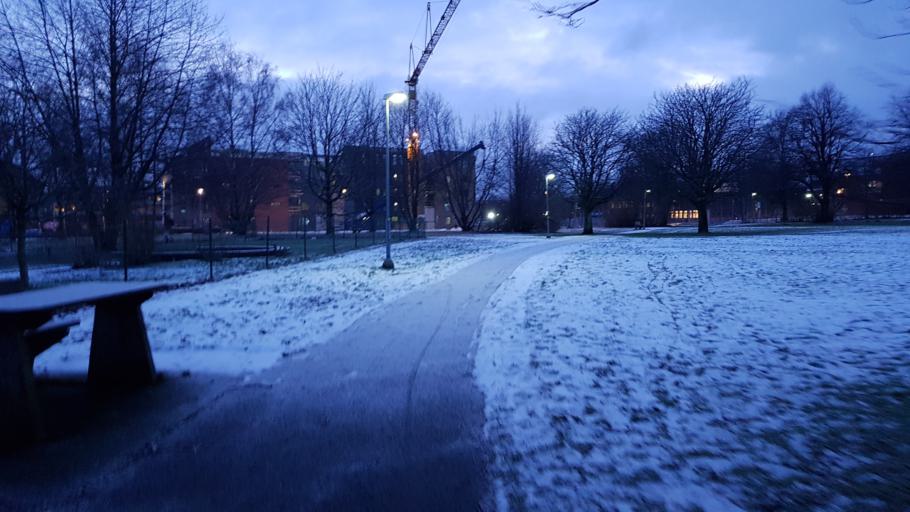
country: SE
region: Vaestra Goetaland
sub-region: Goteborg
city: Majorna
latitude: 57.6655
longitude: 11.9312
